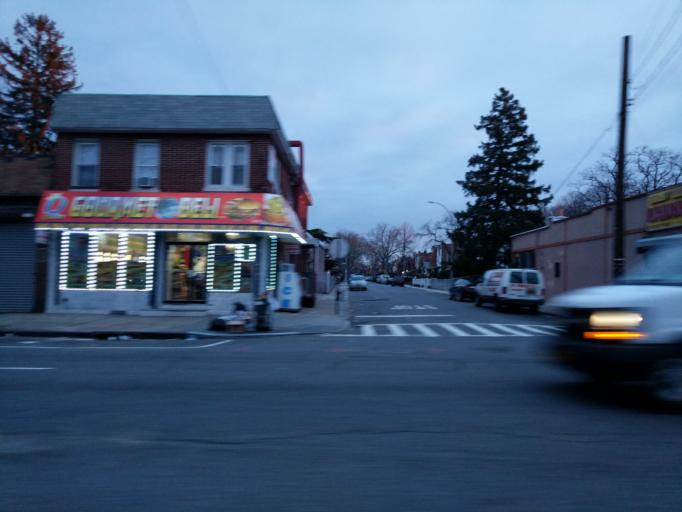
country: US
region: New York
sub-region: Queens County
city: Jamaica
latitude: 40.6822
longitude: -73.7665
